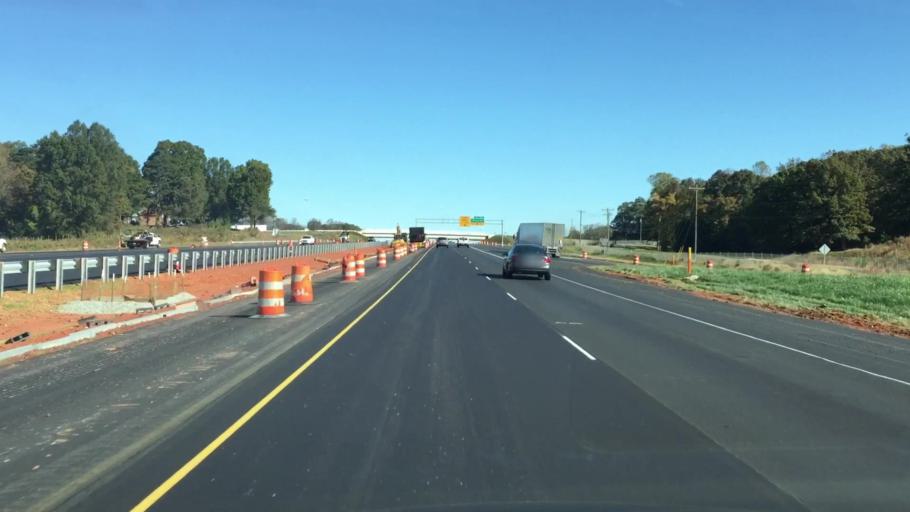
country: US
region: North Carolina
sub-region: Guilford County
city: McLeansville
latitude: 36.1472
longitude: -79.7322
